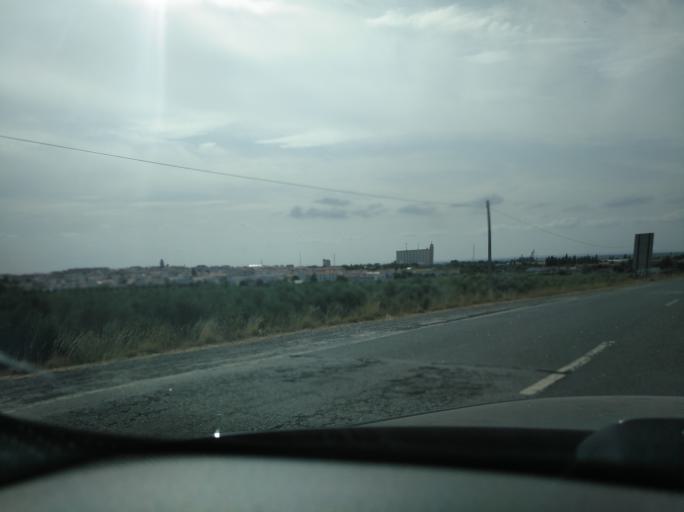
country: PT
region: Beja
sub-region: Beja
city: Ferreira do Alentejo
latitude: 38.0633
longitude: -8.1078
